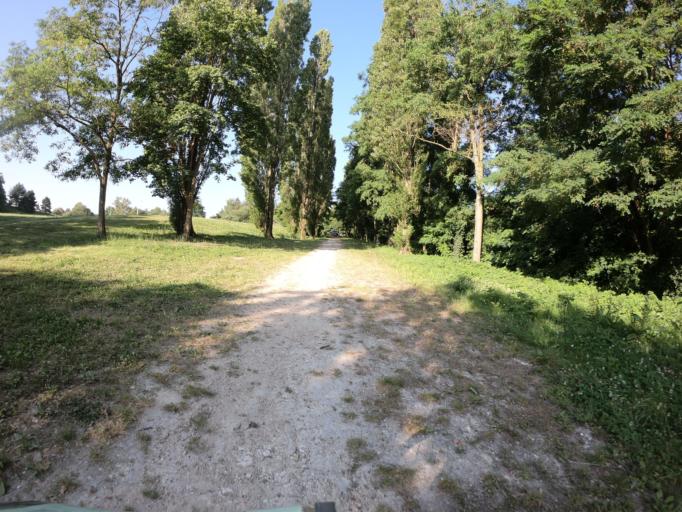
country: FR
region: Ile-de-France
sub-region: Departement de l'Essonne
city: Verrieres-le-Buisson
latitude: 48.7533
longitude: 2.2782
